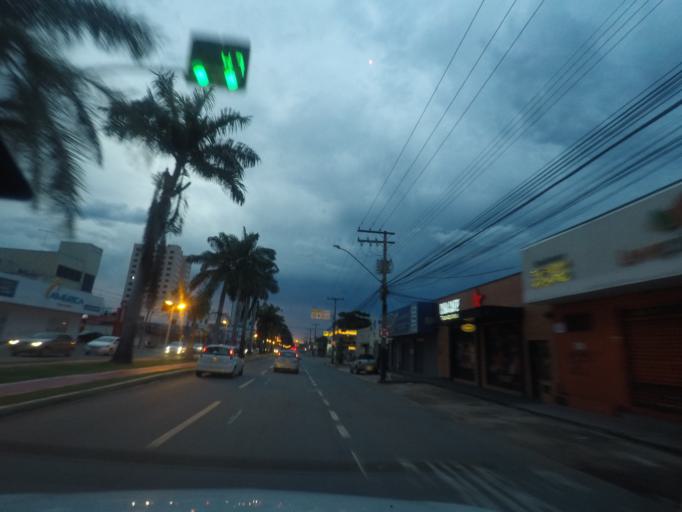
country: BR
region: Goias
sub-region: Goiania
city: Goiania
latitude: -16.7146
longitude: -49.2765
